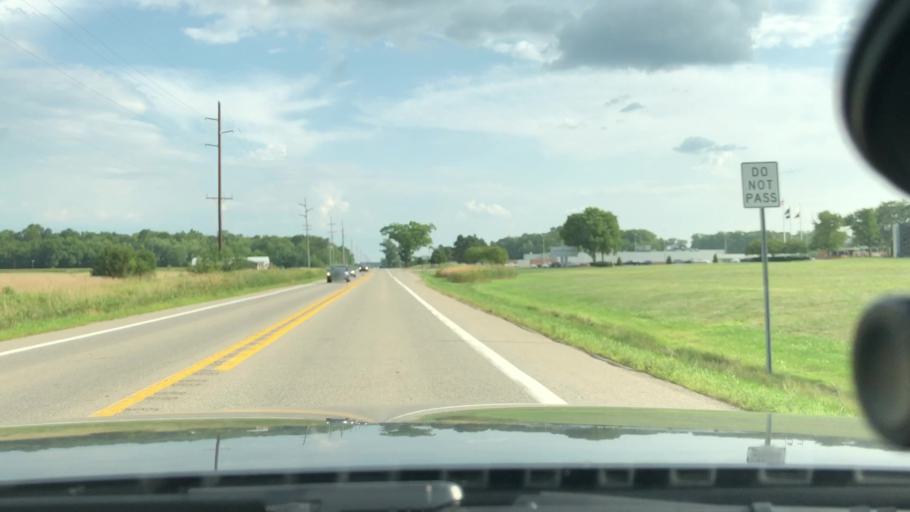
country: US
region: Michigan
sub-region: Washtenaw County
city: Chelsea
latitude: 42.2695
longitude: -84.0342
